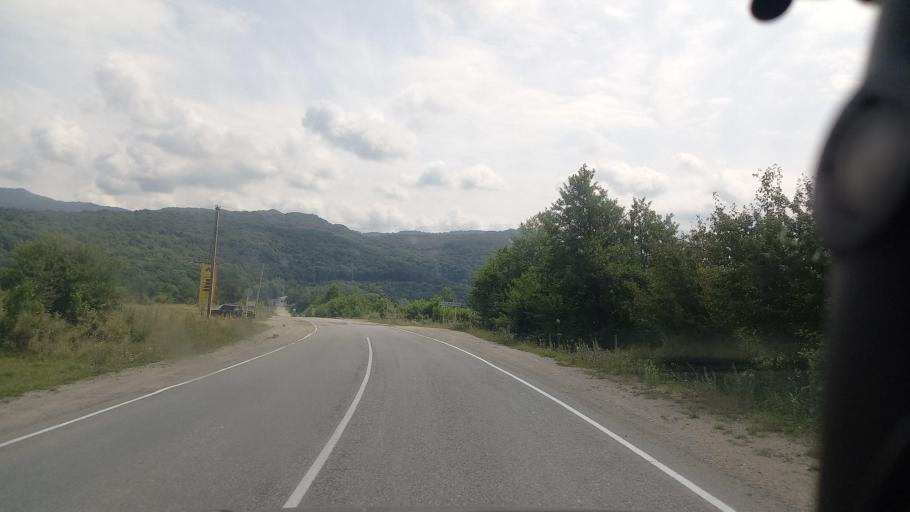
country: RU
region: Karachayevo-Cherkesiya
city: Kurdzhinovo
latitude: 44.0124
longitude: 40.9419
